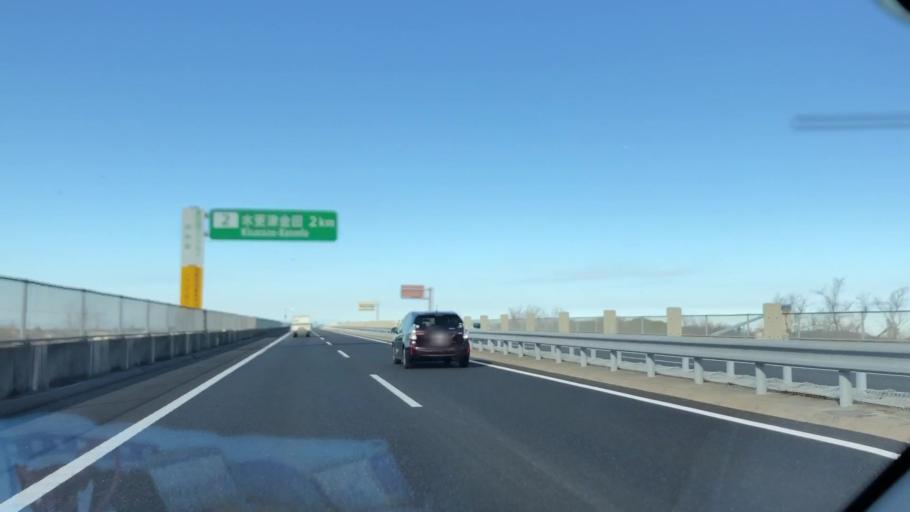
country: JP
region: Chiba
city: Kisarazu
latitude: 35.4167
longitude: 139.9473
